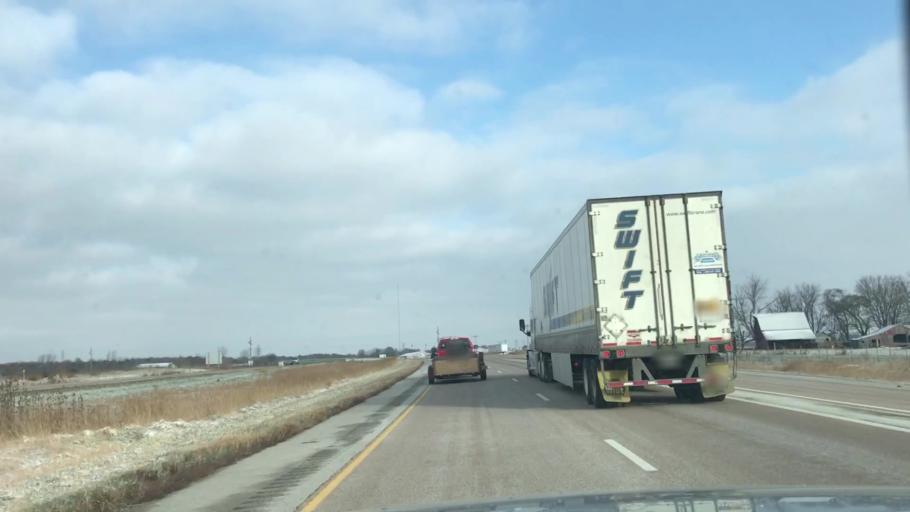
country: US
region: Illinois
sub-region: Macoupin County
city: Staunton
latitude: 39.0246
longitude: -89.7499
